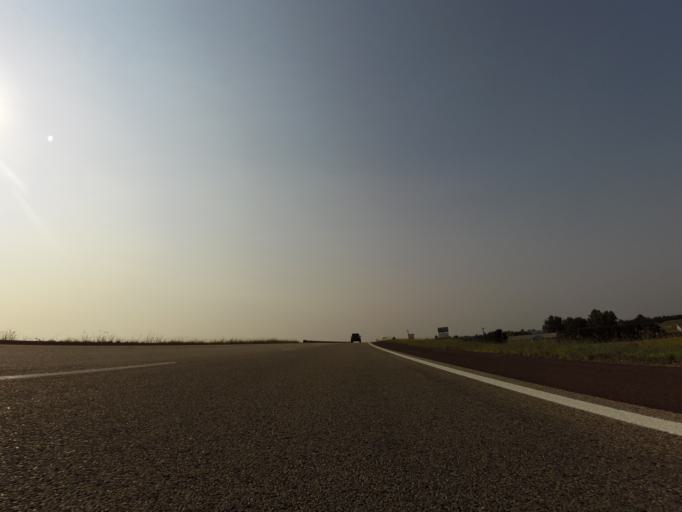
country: US
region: Kansas
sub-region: Reno County
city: Haven
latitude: 37.9395
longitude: -97.8798
